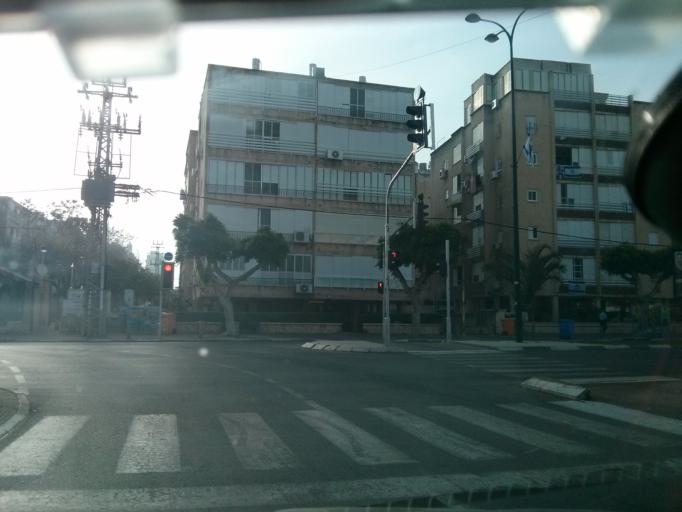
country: IL
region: Central District
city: Netanya
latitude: 32.3236
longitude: 34.8563
